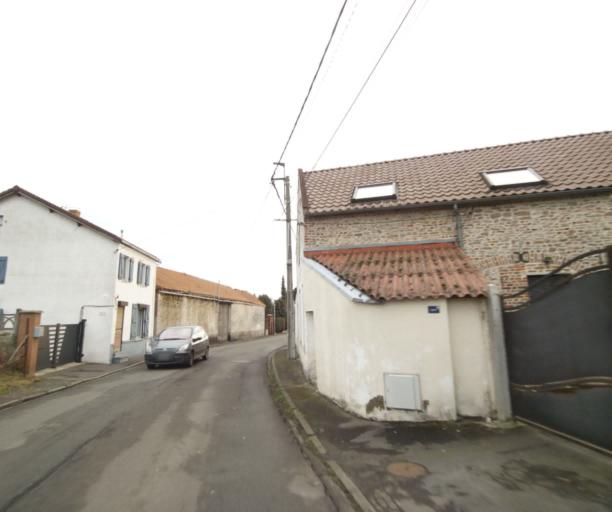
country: FR
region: Nord-Pas-de-Calais
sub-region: Departement du Nord
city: Conde-sur-l'Escaut
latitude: 50.4729
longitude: 3.5853
